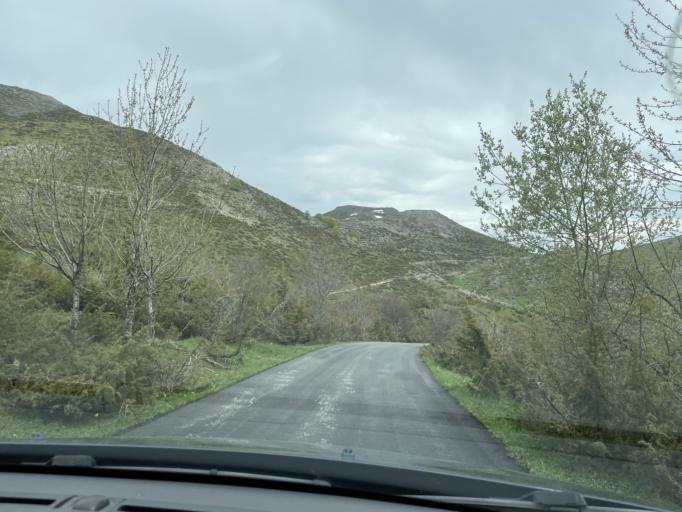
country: MK
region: Opstina Rostusa
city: Rostusha
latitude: 41.6243
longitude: 20.6836
